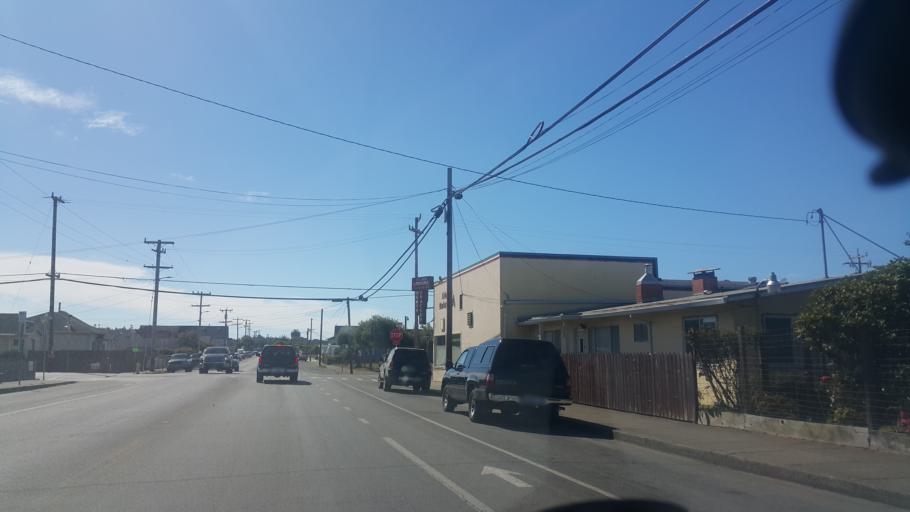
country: US
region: California
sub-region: Mendocino County
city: Fort Bragg
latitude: 39.4422
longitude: -123.7981
